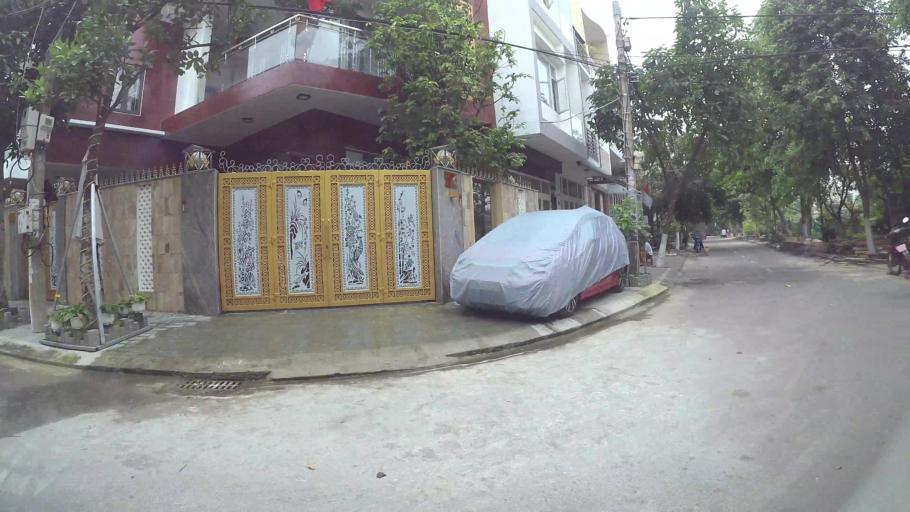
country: VN
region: Da Nang
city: Cam Le
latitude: 16.0371
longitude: 108.2160
